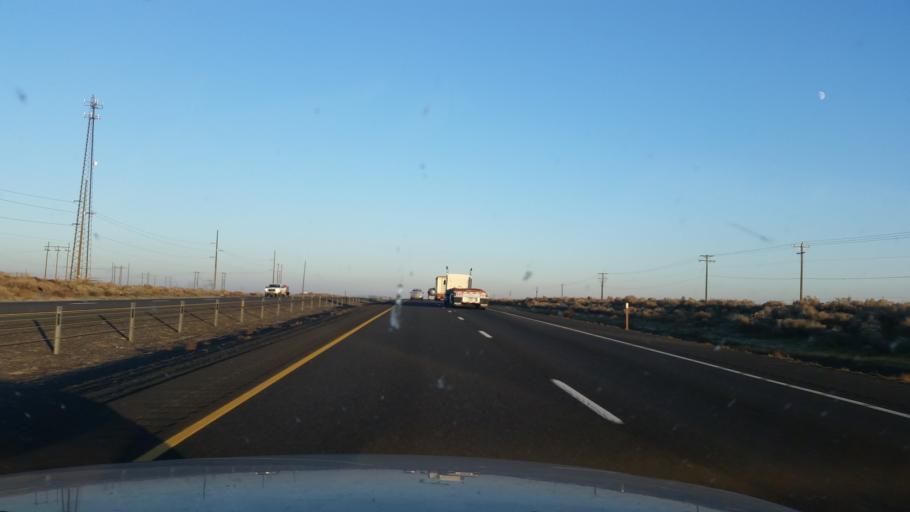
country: US
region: Washington
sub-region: Grant County
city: Cascade Valley
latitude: 47.1041
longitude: -119.5309
